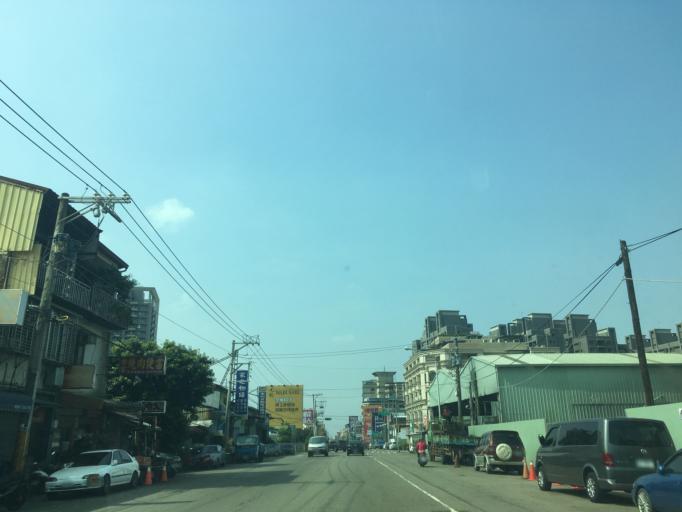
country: TW
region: Taiwan
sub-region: Taichung City
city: Taichung
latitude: 24.1617
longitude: 120.7138
